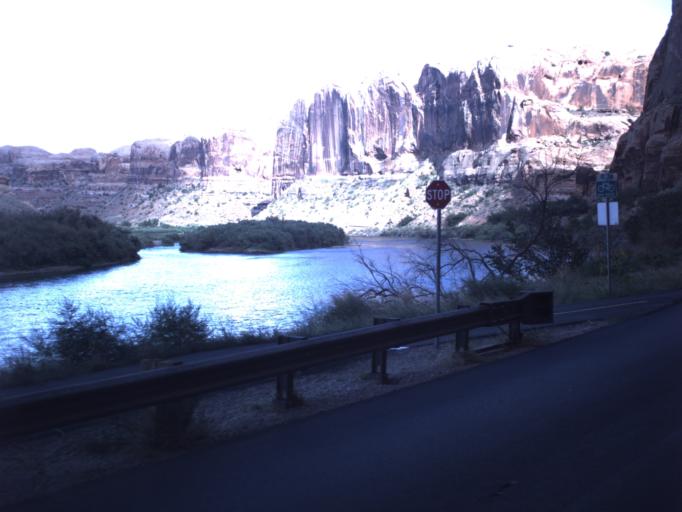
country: US
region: Utah
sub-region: Grand County
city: Moab
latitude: 38.6081
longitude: -109.5463
